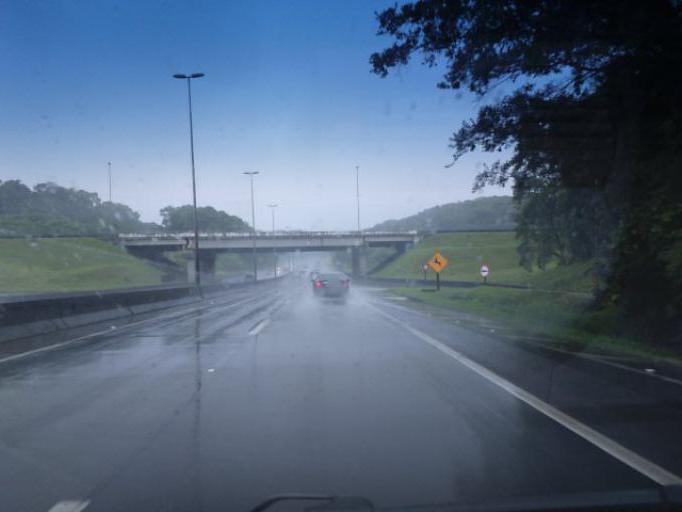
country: BR
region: Santa Catarina
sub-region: Joinville
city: Joinville
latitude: -26.3864
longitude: -48.8444
